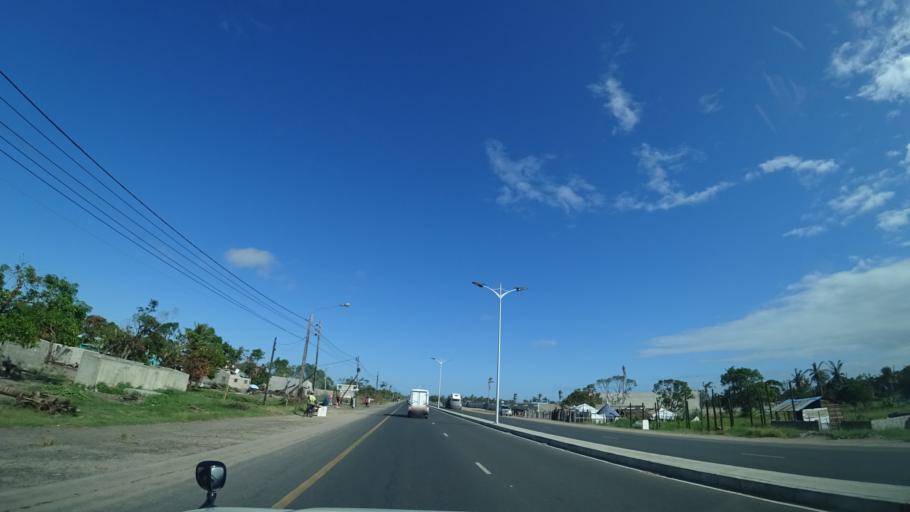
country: MZ
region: Sofala
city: Beira
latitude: -19.7371
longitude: 34.8412
